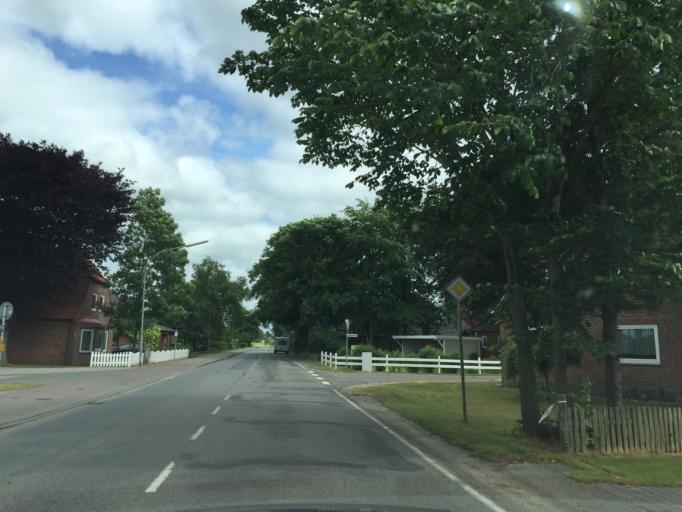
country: DE
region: Schleswig-Holstein
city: Suderlugum
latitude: 54.8702
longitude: 8.8923
